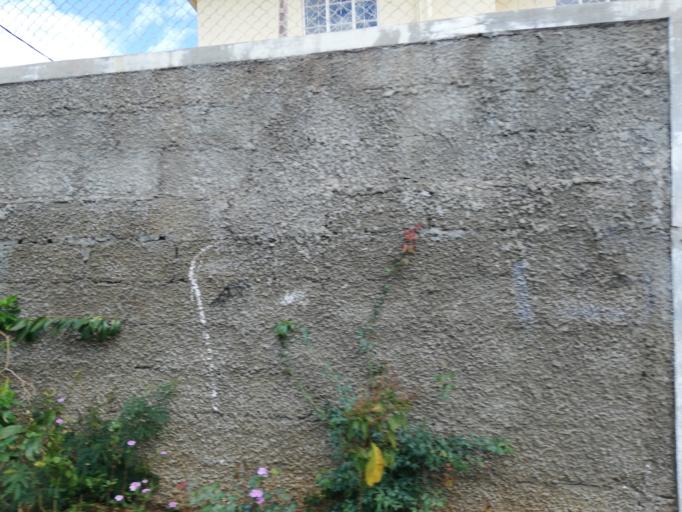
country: MU
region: Moka
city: Pailles
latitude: -20.1971
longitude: 57.4711
